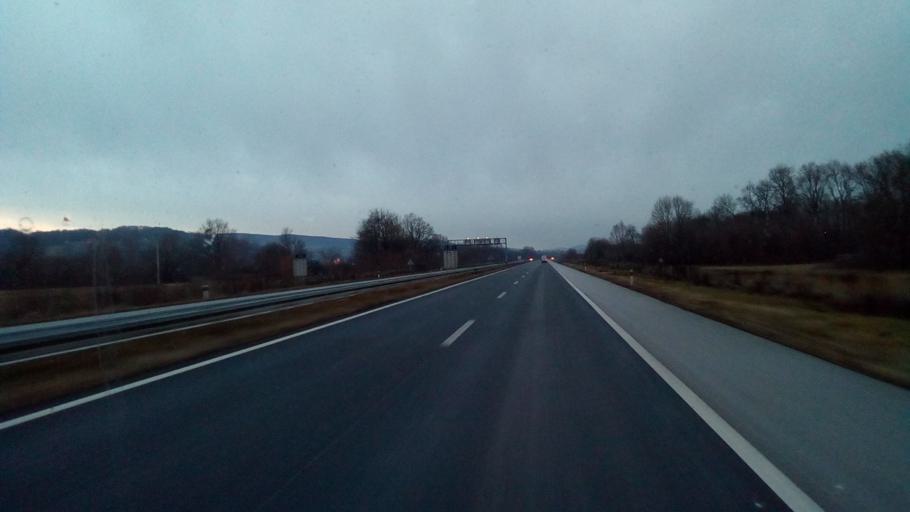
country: HR
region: Zagrebacka
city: Brckovljani
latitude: 45.9296
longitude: 16.2711
